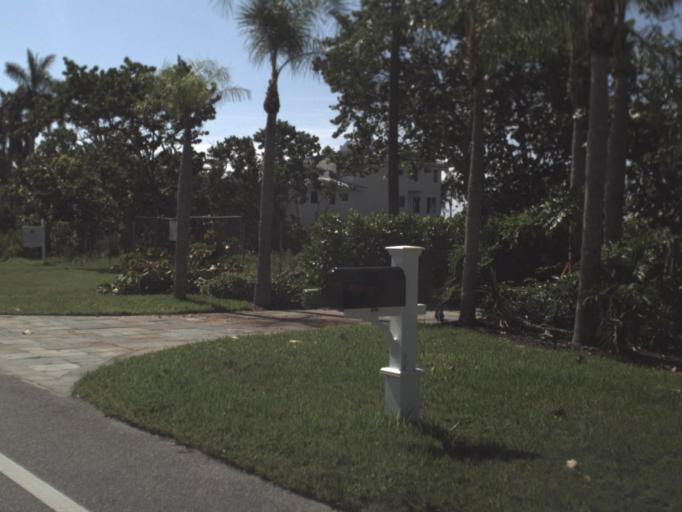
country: US
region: Florida
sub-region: Manatee County
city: Longboat Key
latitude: 27.4246
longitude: -82.6723
